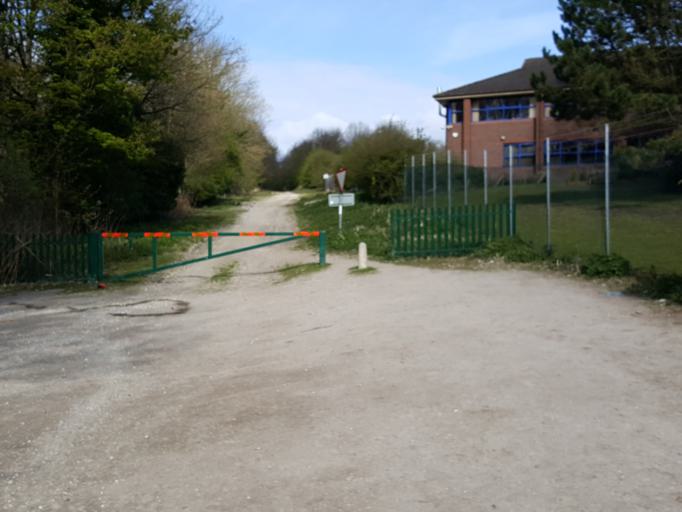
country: GB
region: England
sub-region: East Riding of Yorkshire
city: North Ferriby
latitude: 53.7338
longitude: -0.5244
